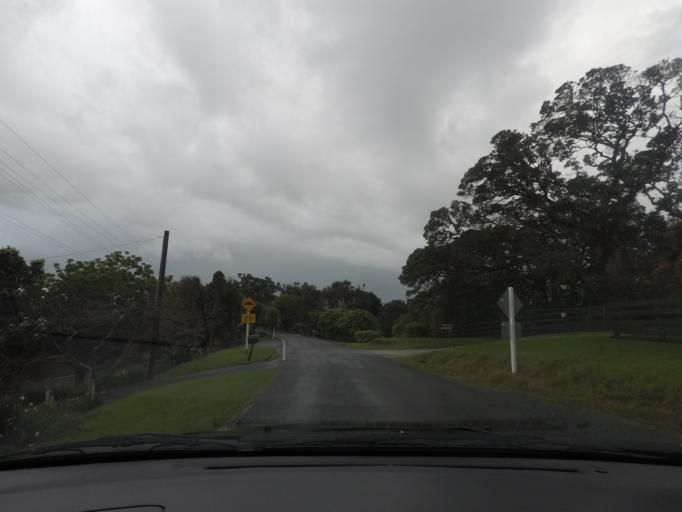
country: NZ
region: Auckland
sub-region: Auckland
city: Warkworth
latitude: -36.4820
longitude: 174.7286
